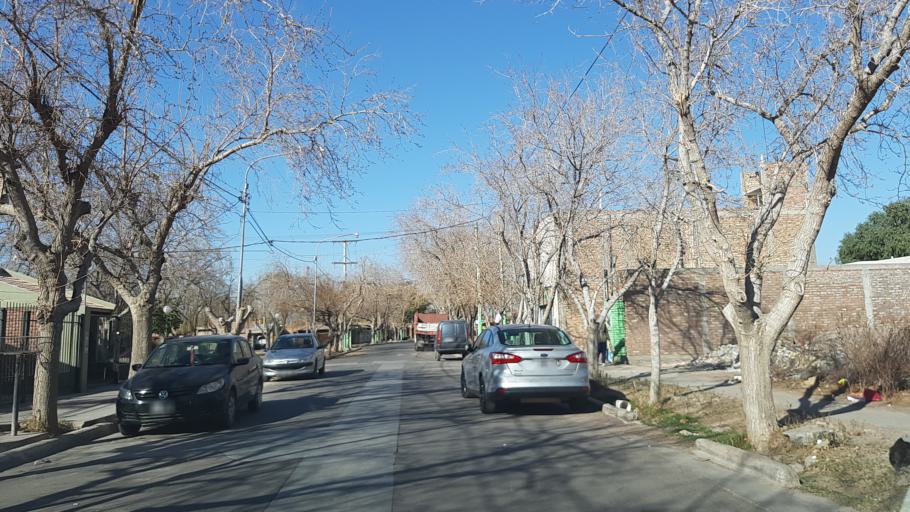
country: AR
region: San Juan
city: San Juan
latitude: -31.5191
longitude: -68.5883
